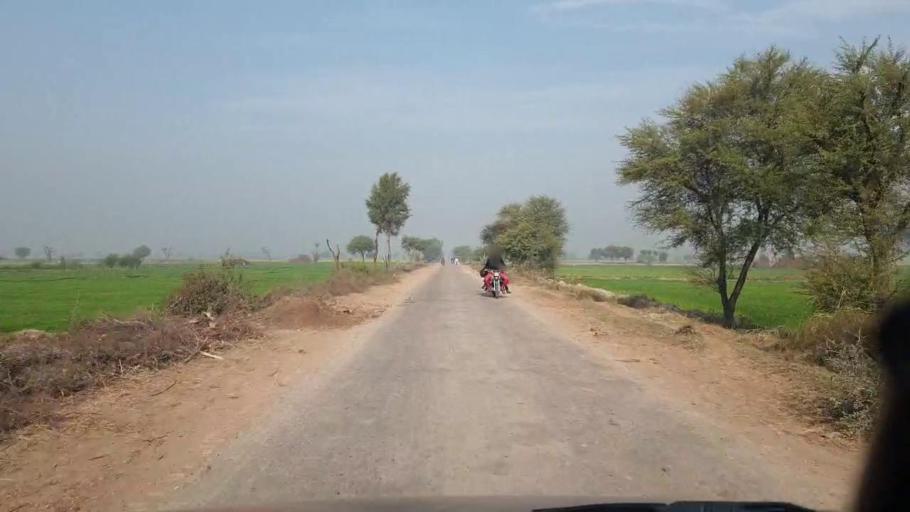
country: PK
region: Sindh
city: Shahdadpur
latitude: 25.9702
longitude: 68.5793
